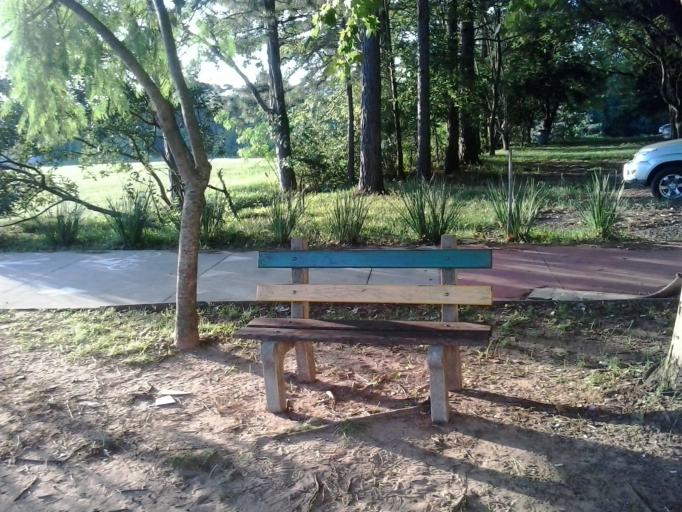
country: BR
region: Rio Grande do Sul
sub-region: Santa Maria
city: Santa Maria
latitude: -29.7198
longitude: -53.7106
